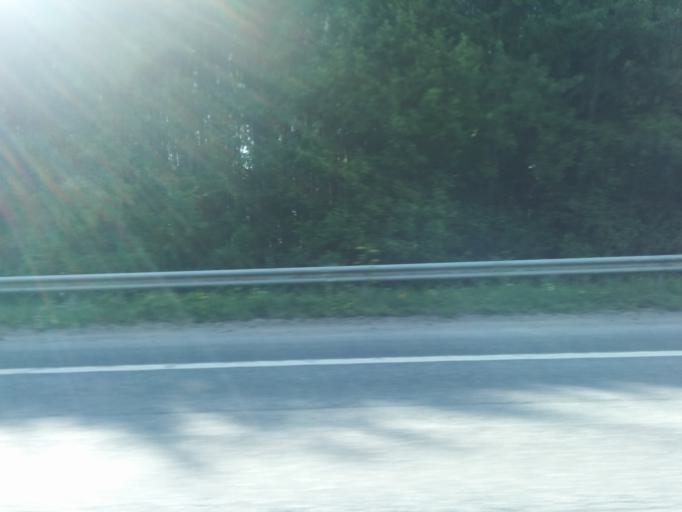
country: FI
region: Pirkanmaa
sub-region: Tampere
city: Tampere
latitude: 61.5232
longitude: 23.9280
